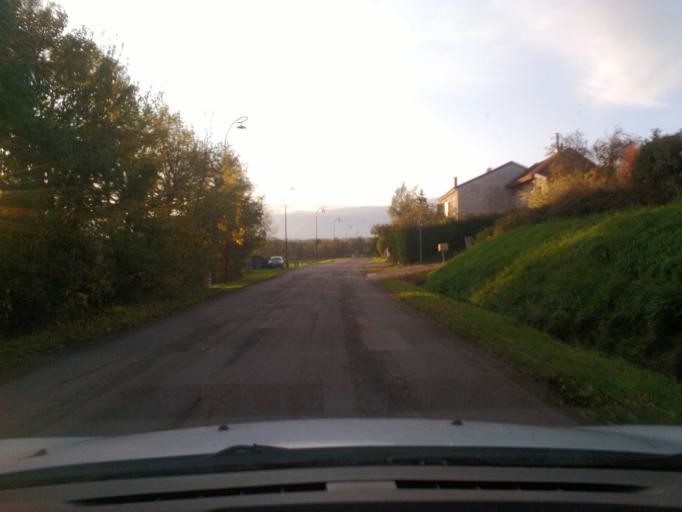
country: FR
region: Lorraine
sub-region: Departement des Vosges
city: Mirecourt
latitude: 48.2579
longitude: 6.1864
